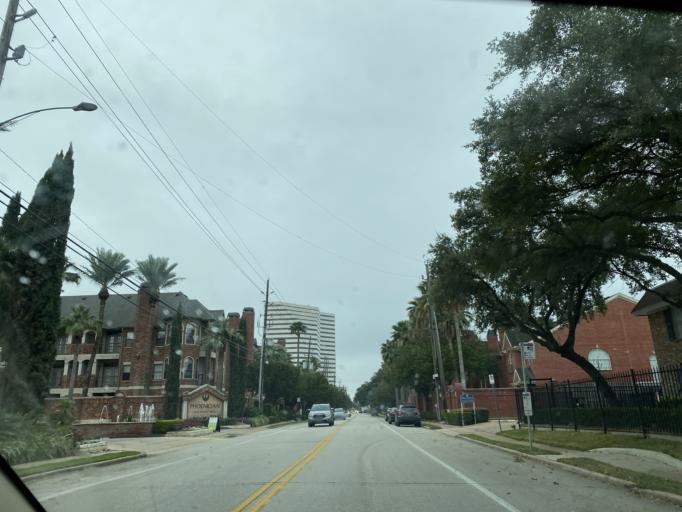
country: US
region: Texas
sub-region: Harris County
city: Hunters Creek Village
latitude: 29.7428
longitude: -95.4795
